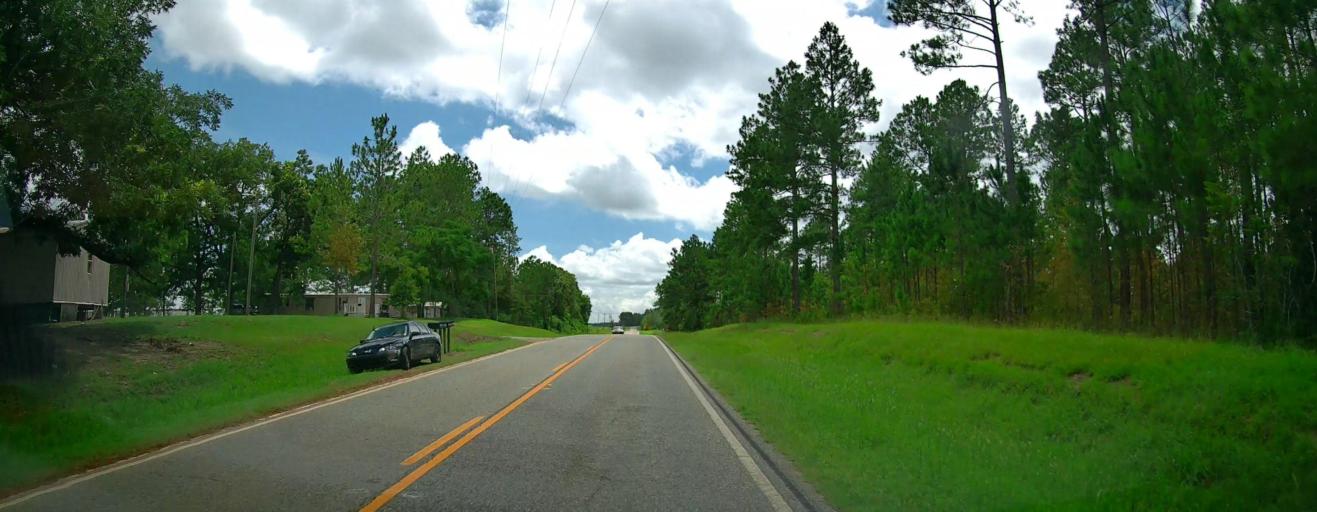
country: US
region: Georgia
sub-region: Wilcox County
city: Rochelle
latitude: 31.9039
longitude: -83.5532
